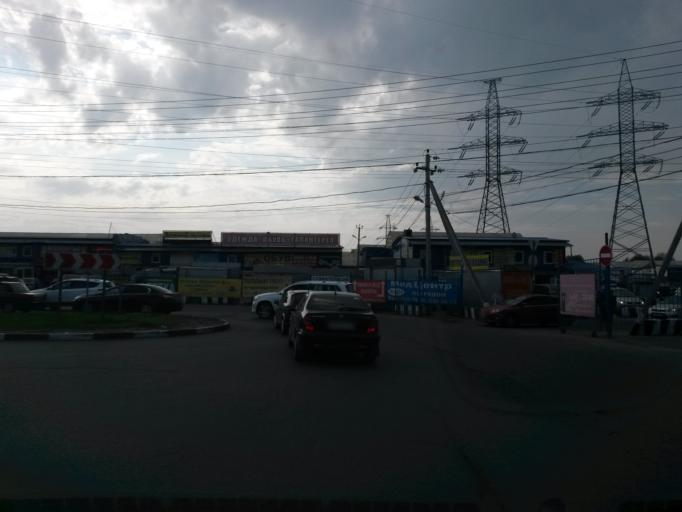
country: RU
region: Moscow
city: Tyoply Stan
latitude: 55.6054
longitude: 37.4816
